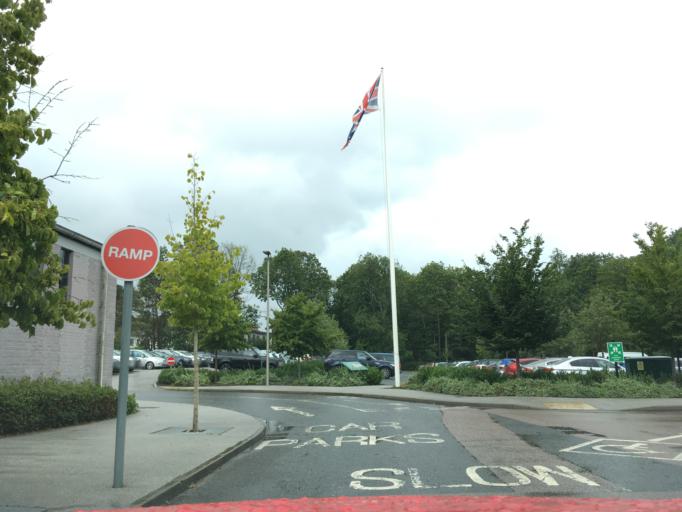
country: GB
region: England
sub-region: Buckinghamshire
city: Bletchley
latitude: 51.9976
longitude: -0.7391
